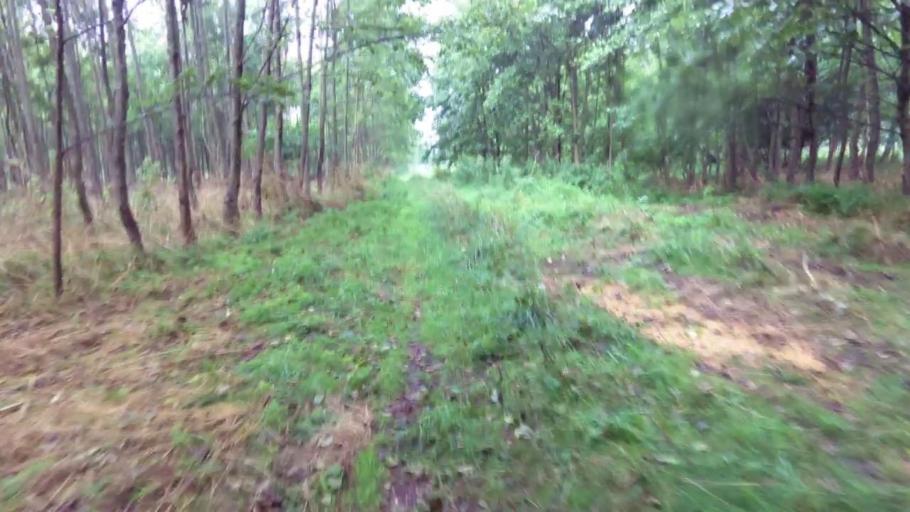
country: PL
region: West Pomeranian Voivodeship
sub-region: Powiat choszczenski
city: Choszczno
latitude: 53.2405
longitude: 15.4491
